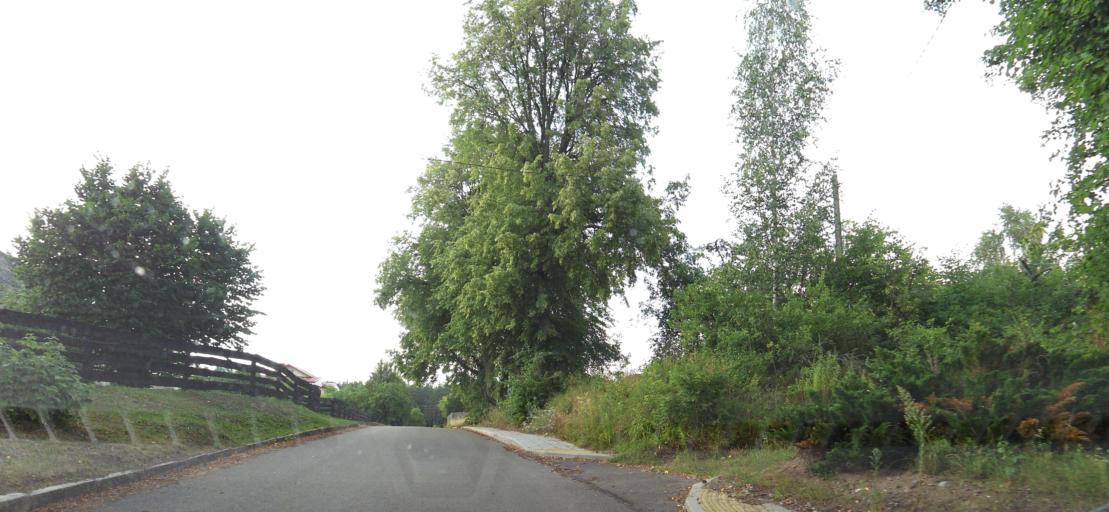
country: LT
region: Alytaus apskritis
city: Varena
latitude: 54.2176
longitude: 24.4178
